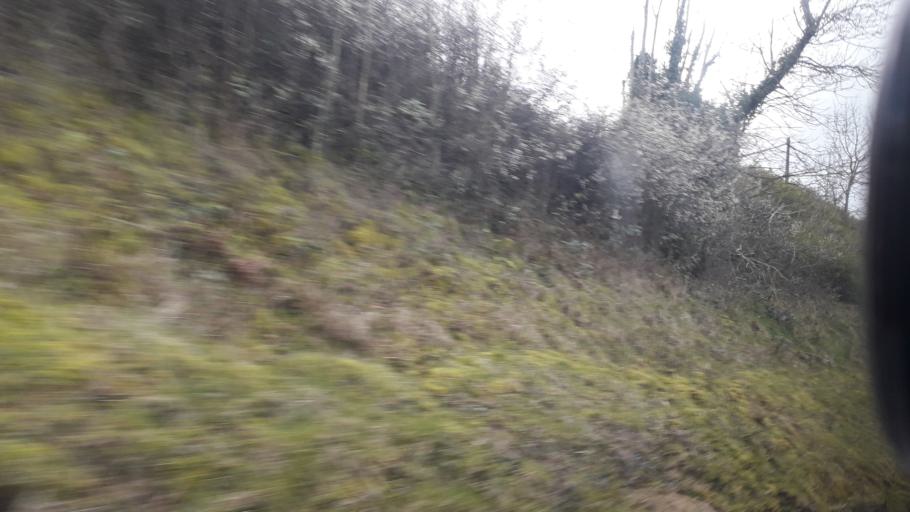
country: IE
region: Leinster
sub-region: An Iarmhi
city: Rathwire
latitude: 53.4950
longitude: -7.1746
